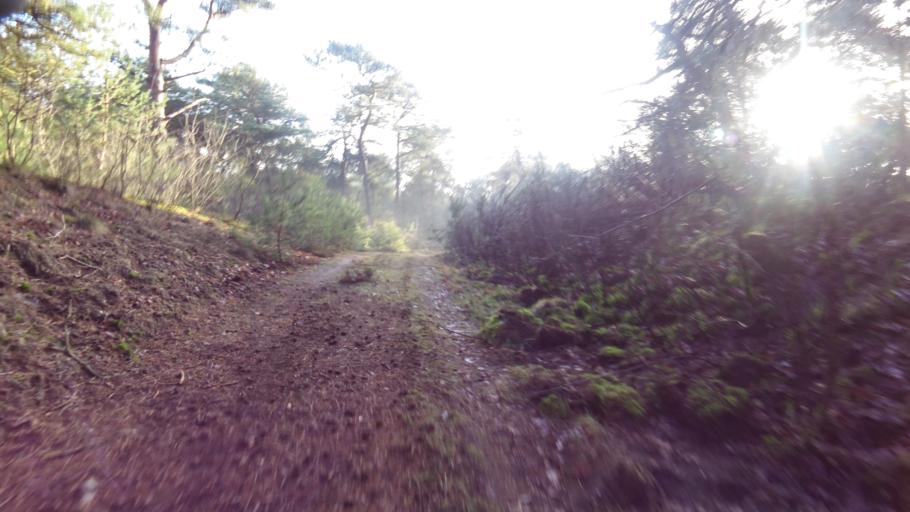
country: NL
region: Gelderland
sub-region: Gemeente Barneveld
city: Garderen
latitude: 52.2036
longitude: 5.7383
